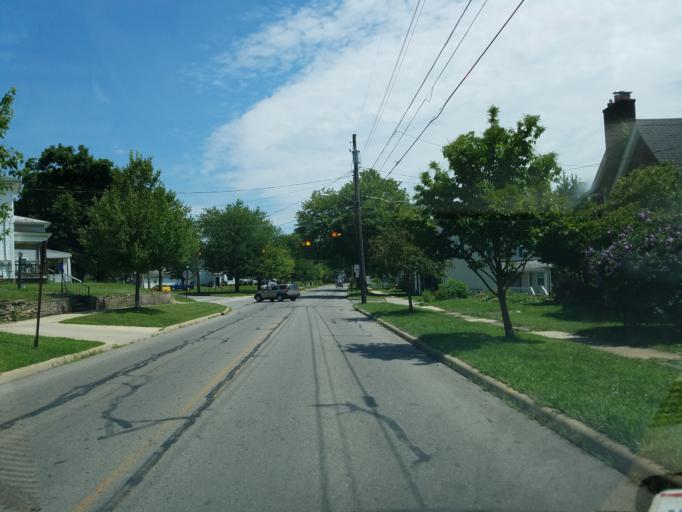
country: US
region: Ohio
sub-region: Ashland County
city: Ashland
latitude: 40.8718
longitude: -82.3226
